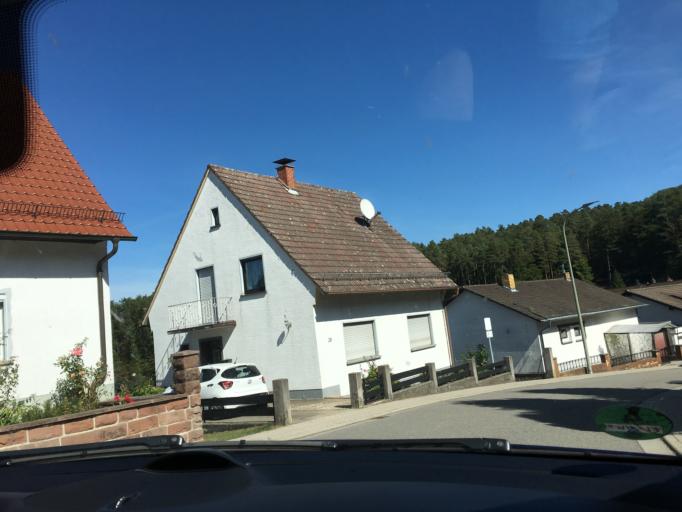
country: DE
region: Rheinland-Pfalz
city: Schopp
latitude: 49.3532
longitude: 7.6917
